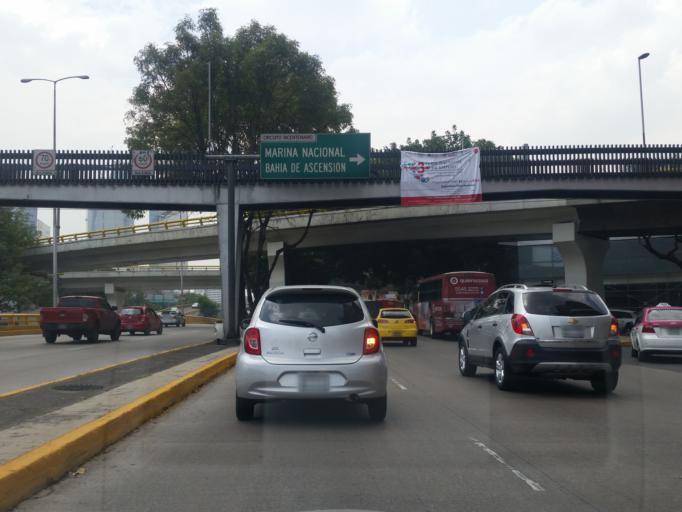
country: MX
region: Mexico City
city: Cuauhtemoc
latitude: 19.4346
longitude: -99.1710
